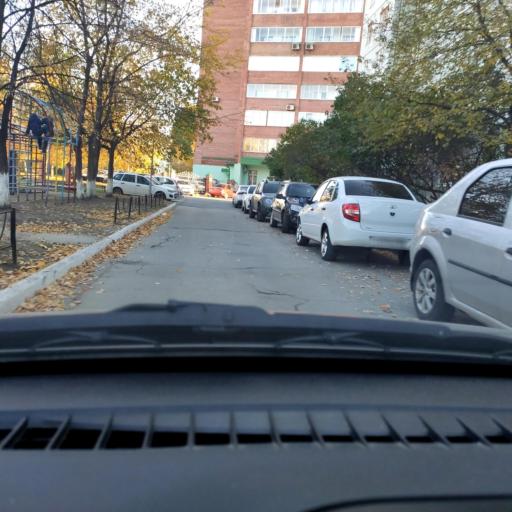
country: RU
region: Samara
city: Tol'yatti
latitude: 53.5437
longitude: 49.3414
